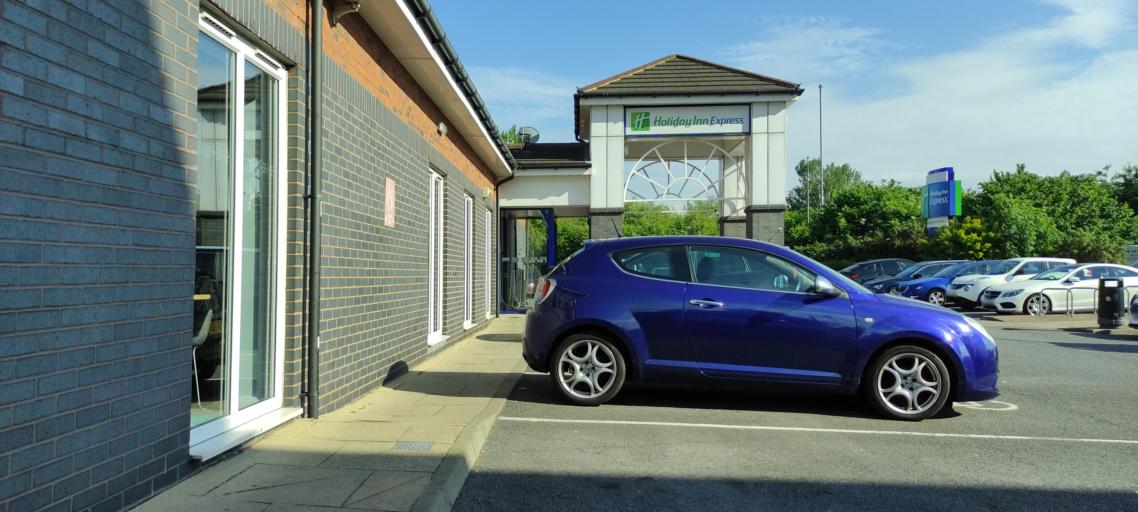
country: GB
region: England
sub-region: Newcastle upon Tyne
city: Benwell
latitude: 54.9631
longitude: -1.6817
